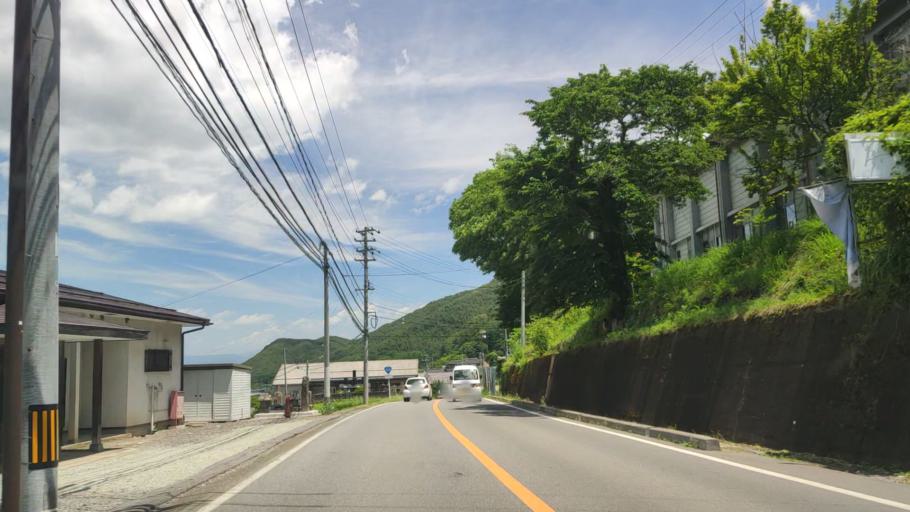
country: JP
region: Nagano
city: Kamimaruko
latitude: 36.2172
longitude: 138.2499
